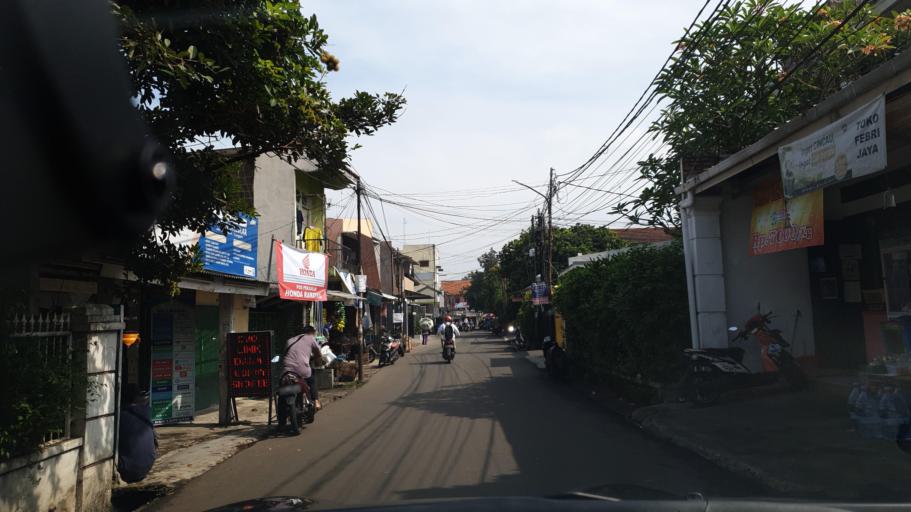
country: ID
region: West Java
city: Pamulang
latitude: -6.3045
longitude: 106.7655
